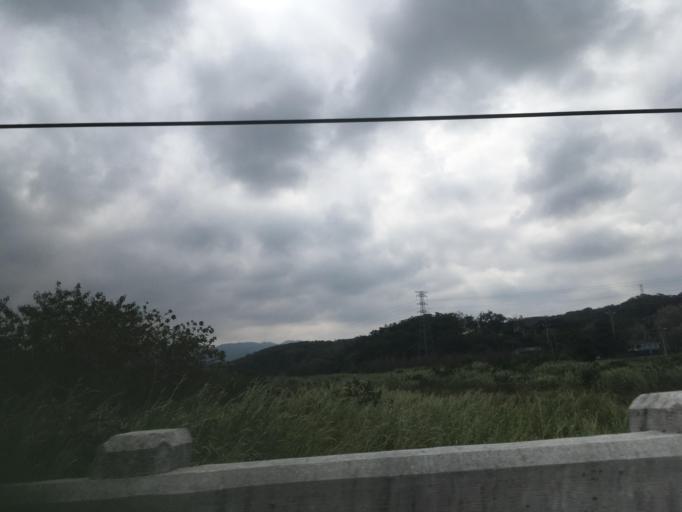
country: TW
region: Taiwan
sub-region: Miaoli
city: Miaoli
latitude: 24.4473
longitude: 120.7190
